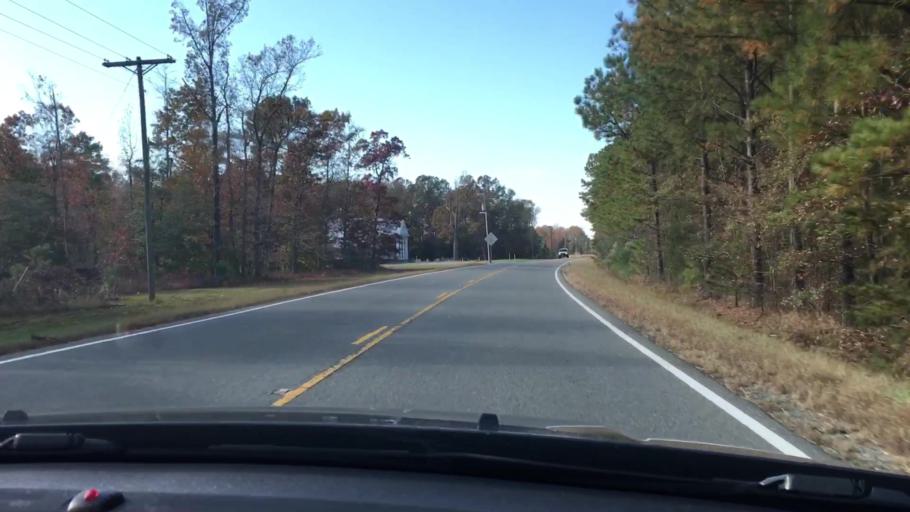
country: US
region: Virginia
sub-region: Hanover County
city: Hanover
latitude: 37.8270
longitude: -77.3432
